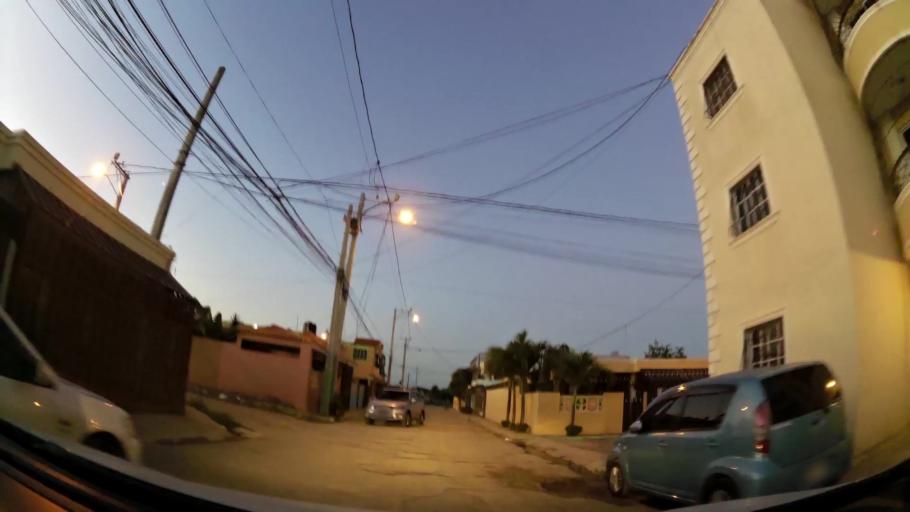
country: DO
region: Santo Domingo
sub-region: Santo Domingo
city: Santo Domingo Este
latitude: 18.5022
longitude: -69.8374
